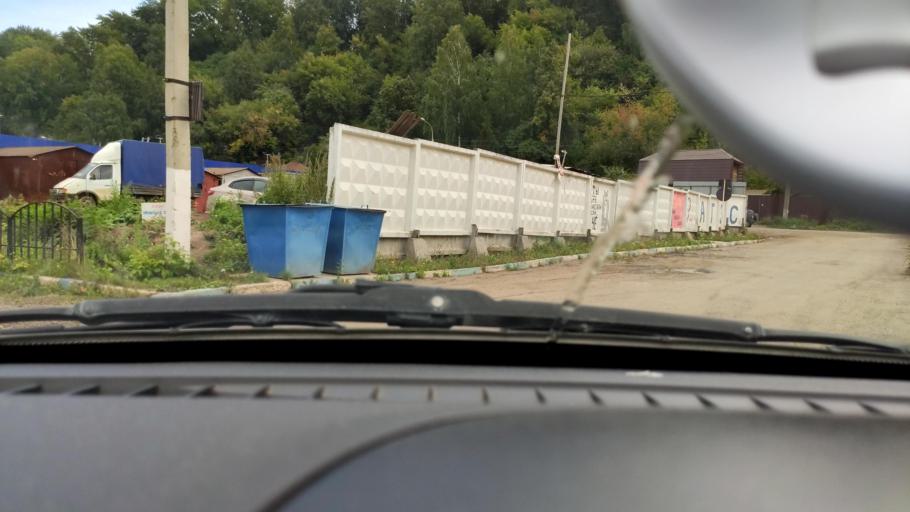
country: RU
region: Perm
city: Perm
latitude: 58.0491
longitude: 56.3239
